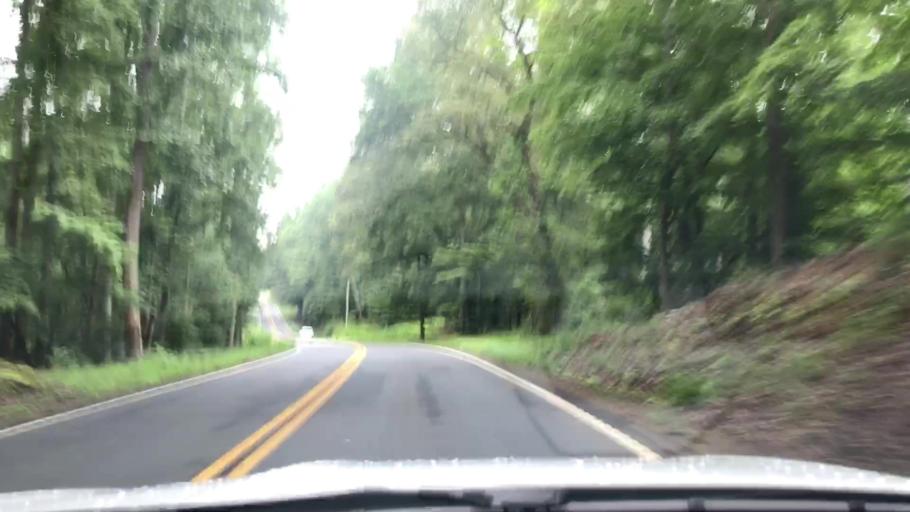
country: US
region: South Carolina
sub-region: Spartanburg County
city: Roebuck
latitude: 34.8247
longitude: -81.9428
